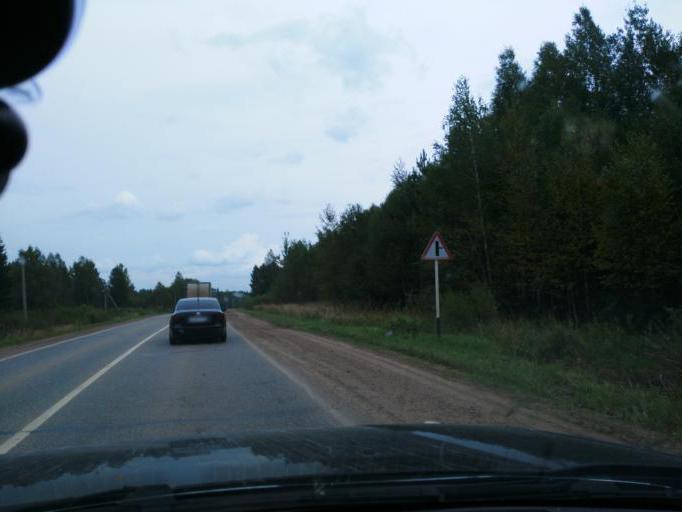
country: RU
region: Bashkortostan
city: Verkhniye Tatyshly
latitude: 56.4970
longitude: 55.8316
